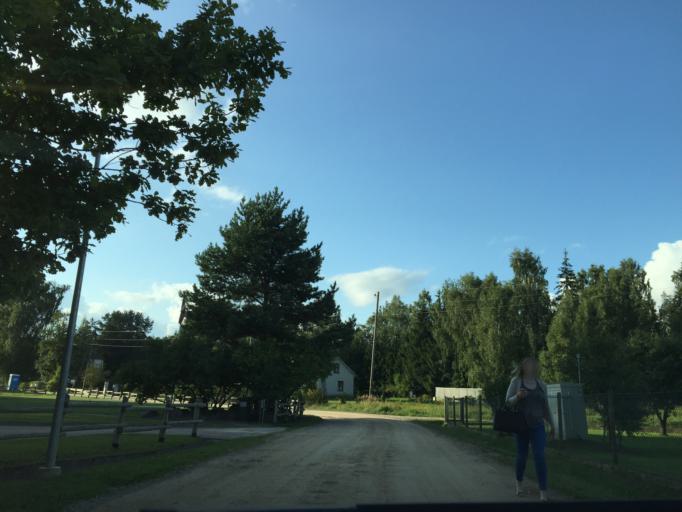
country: LV
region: Ikskile
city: Ikskile
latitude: 56.8369
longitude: 24.5126
